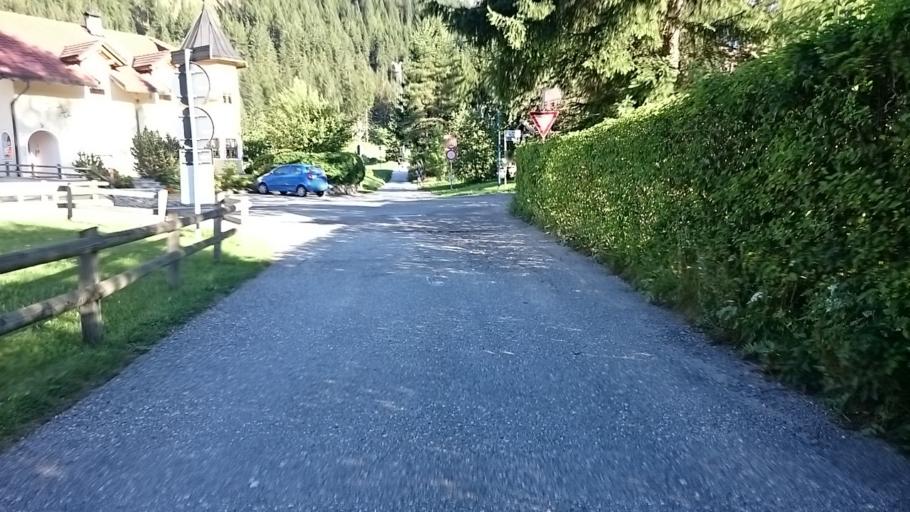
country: IT
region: Trentino-Alto Adige
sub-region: Bolzano
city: Dobbiaco
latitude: 46.7201
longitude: 12.2224
